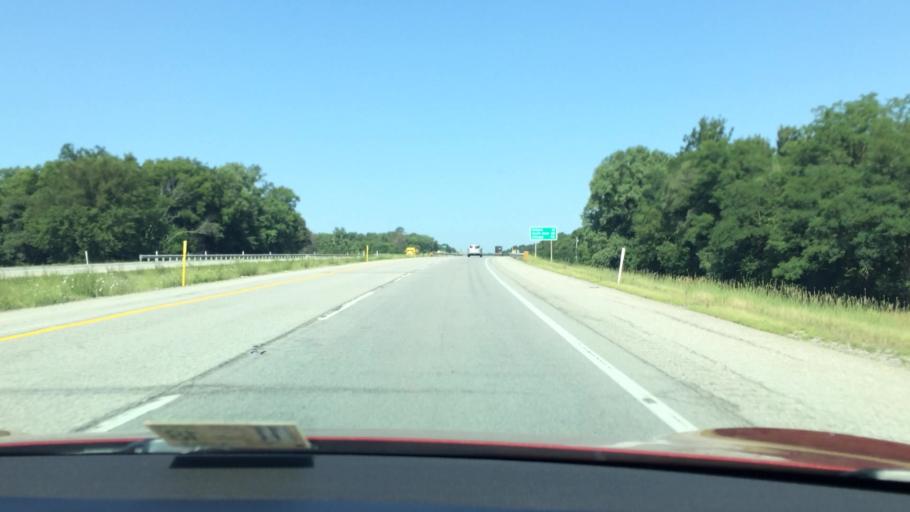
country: US
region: Indiana
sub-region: Elkhart County
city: Bristol
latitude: 41.7345
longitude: -85.8067
